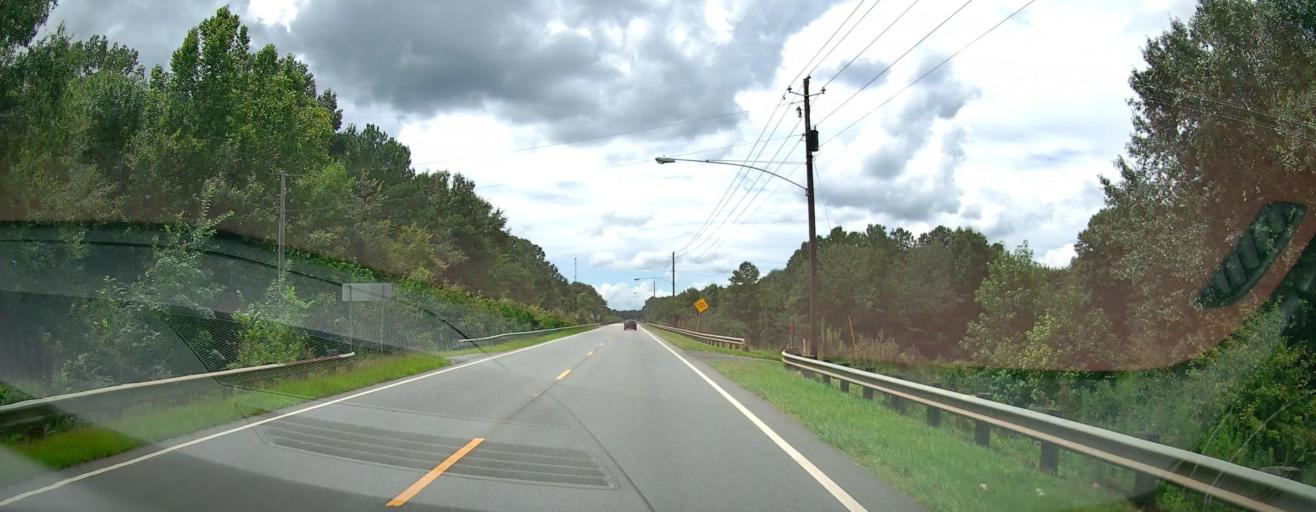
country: US
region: Georgia
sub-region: Macon County
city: Montezuma
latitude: 32.2932
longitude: -84.0387
